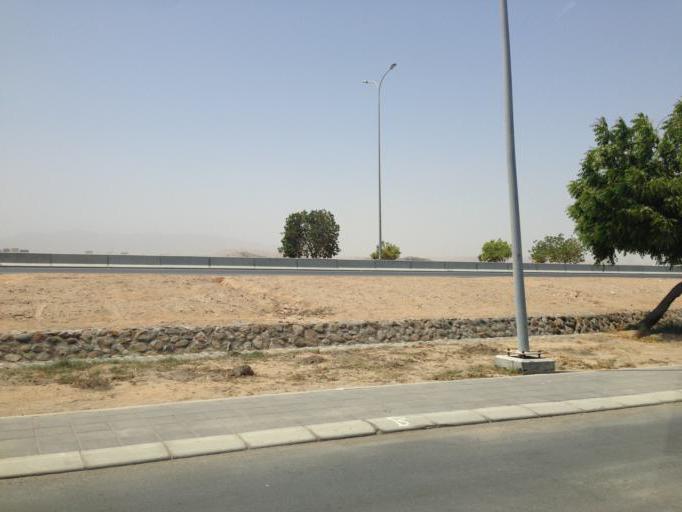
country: OM
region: Muhafazat Masqat
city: Bawshar
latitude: 23.6031
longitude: 58.3438
